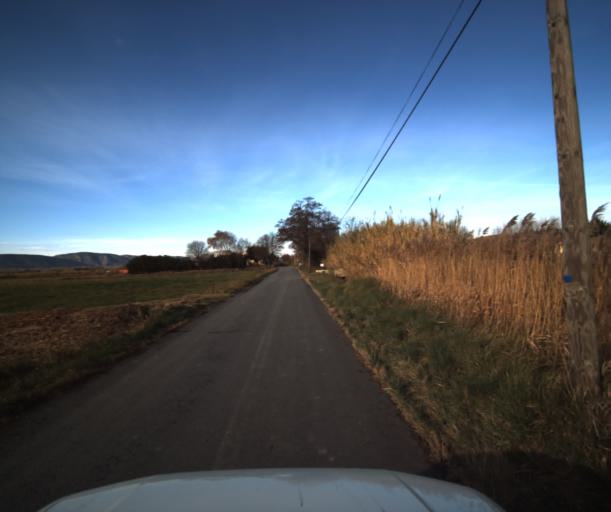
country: FR
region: Provence-Alpes-Cote d'Azur
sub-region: Departement des Bouches-du-Rhone
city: Le Puy-Sainte-Reparade
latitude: 43.6874
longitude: 5.4525
